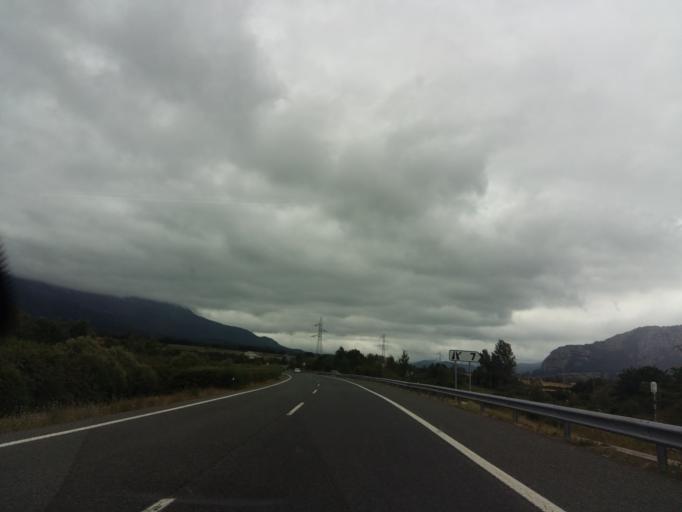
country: ES
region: Navarre
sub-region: Provincia de Navarra
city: Iraneta
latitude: 42.9159
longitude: -1.9157
